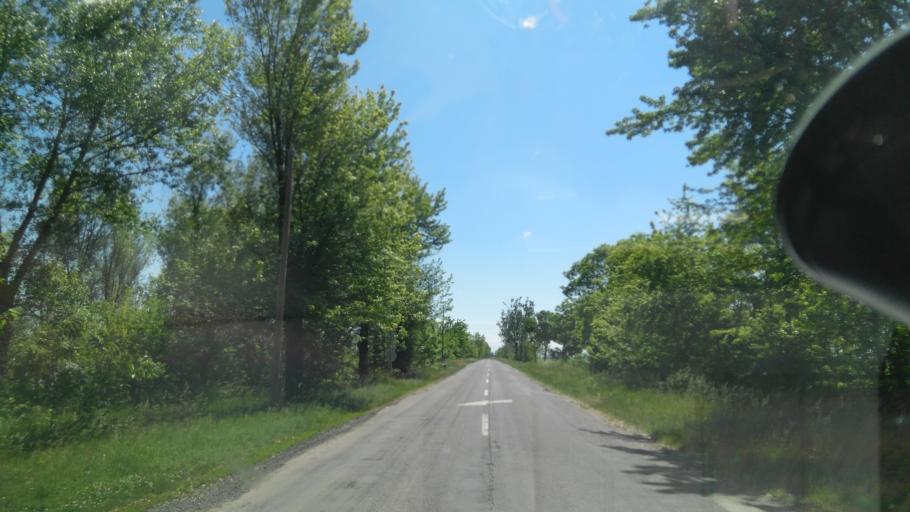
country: HU
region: Bekes
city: Kunagota
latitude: 46.4140
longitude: 21.0448
